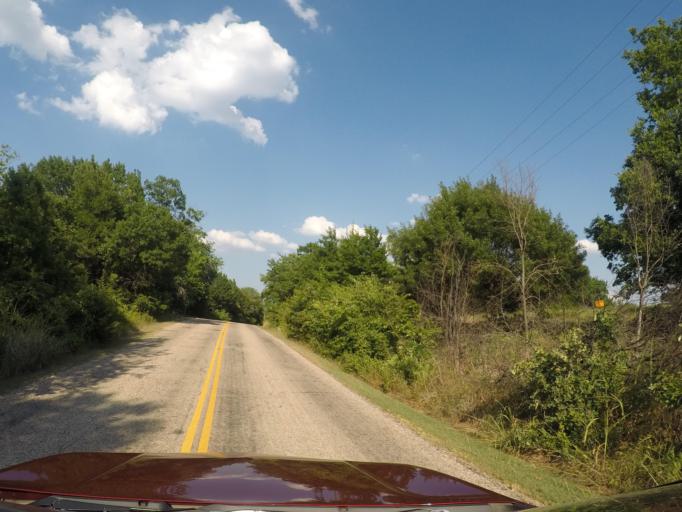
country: US
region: Texas
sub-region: Grayson County
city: Preston
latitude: 33.8183
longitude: -96.6120
